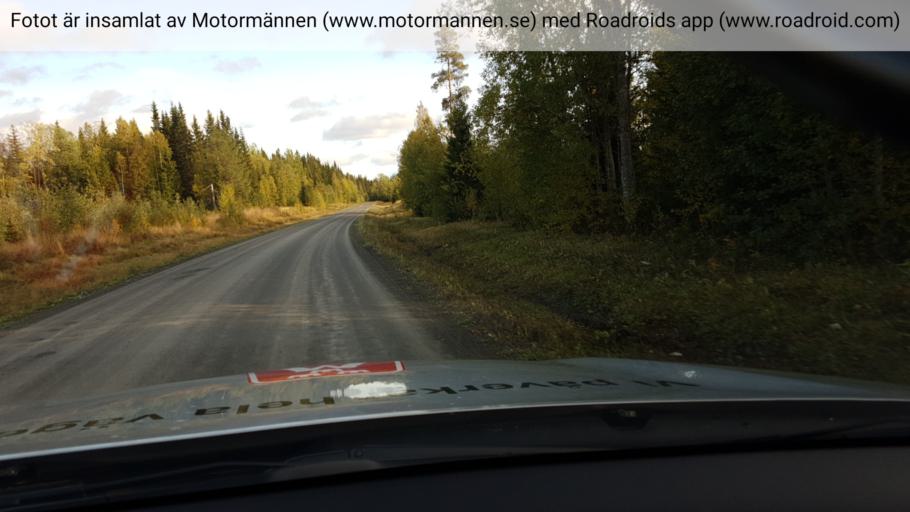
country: SE
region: Jaemtland
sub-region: Krokoms Kommun
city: Krokom
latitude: 63.7025
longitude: 14.5493
